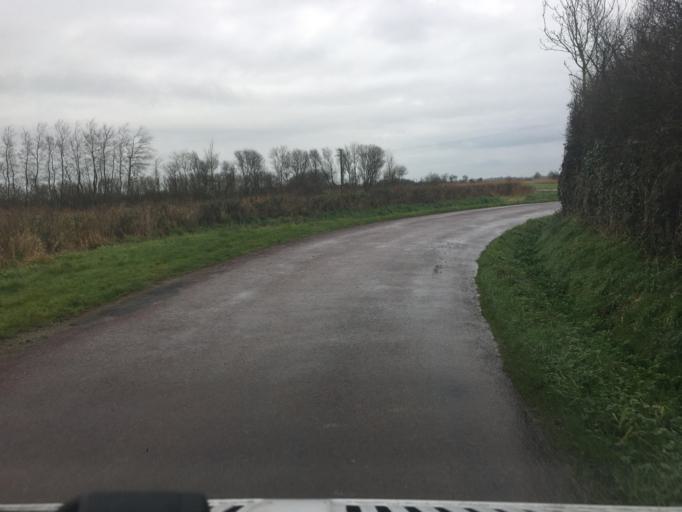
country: FR
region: Lower Normandy
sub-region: Departement de la Manche
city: Sainte-Mere-Eglise
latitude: 49.4412
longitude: -1.2497
